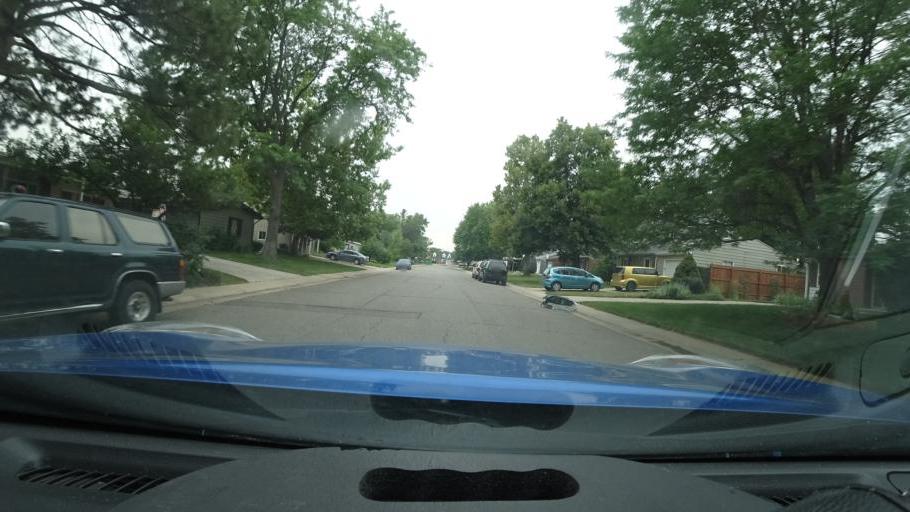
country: US
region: Colorado
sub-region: Arapahoe County
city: Glendale
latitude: 39.6817
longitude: -104.9170
